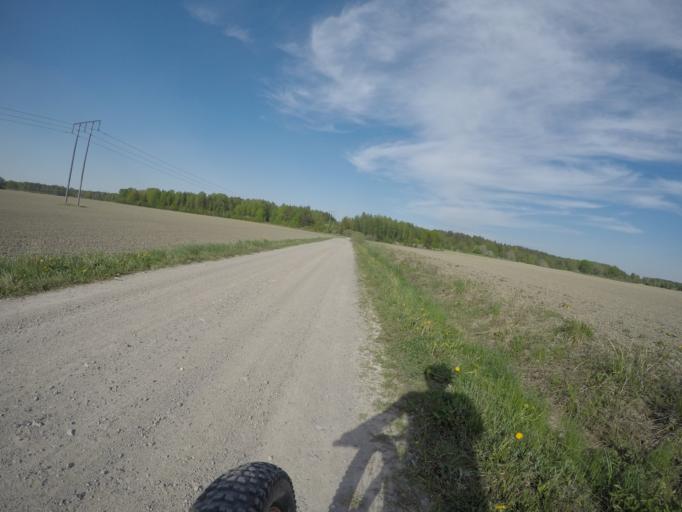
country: SE
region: Vaestmanland
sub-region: Vasteras
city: Vasteras
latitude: 59.6560
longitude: 16.4959
